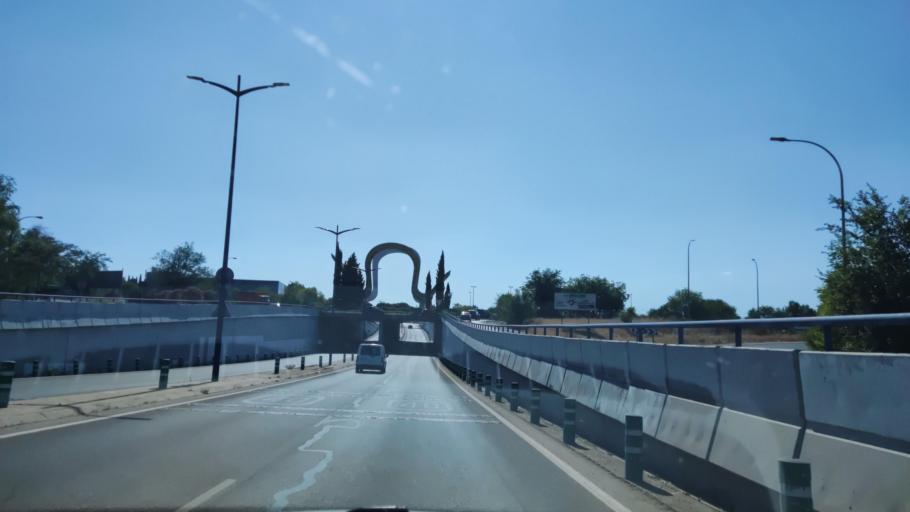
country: ES
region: Madrid
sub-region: Provincia de Madrid
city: Leganes
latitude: 40.3471
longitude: -3.7534
